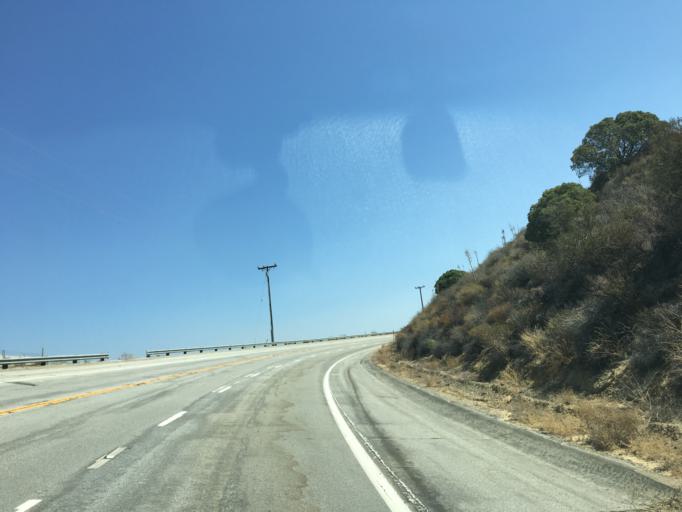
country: US
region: California
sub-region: Los Angeles County
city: Castaic
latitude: 34.5178
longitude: -118.5958
